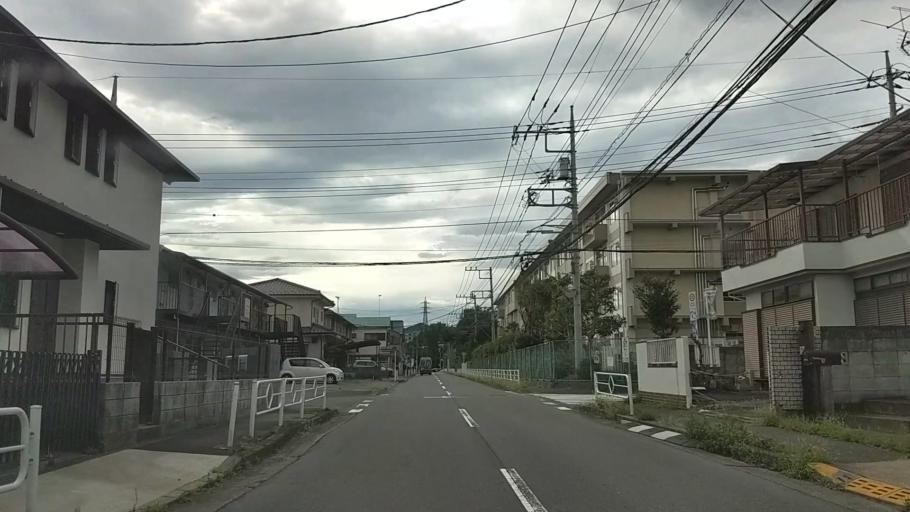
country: JP
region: Tokyo
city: Hachioji
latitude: 35.6362
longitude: 139.3036
